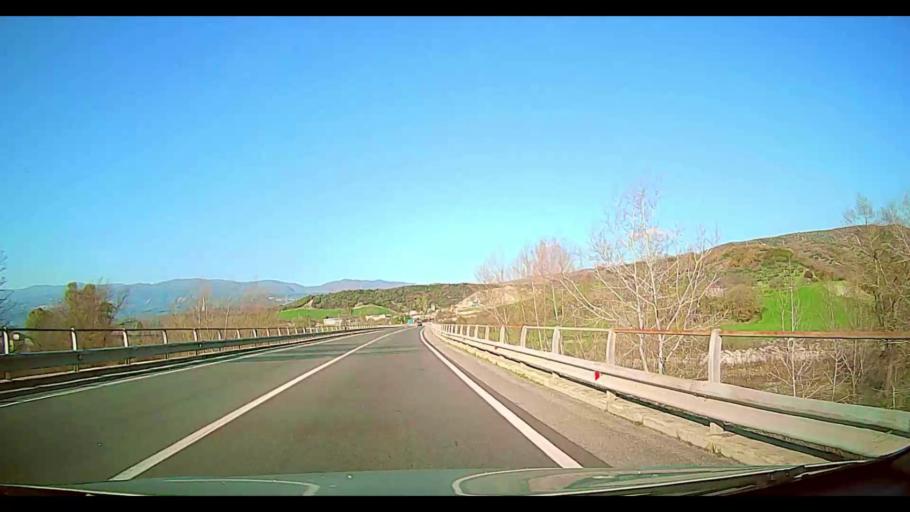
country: IT
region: Calabria
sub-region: Provincia di Crotone
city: Belvedere Spinello
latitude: 39.1877
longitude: 16.8538
